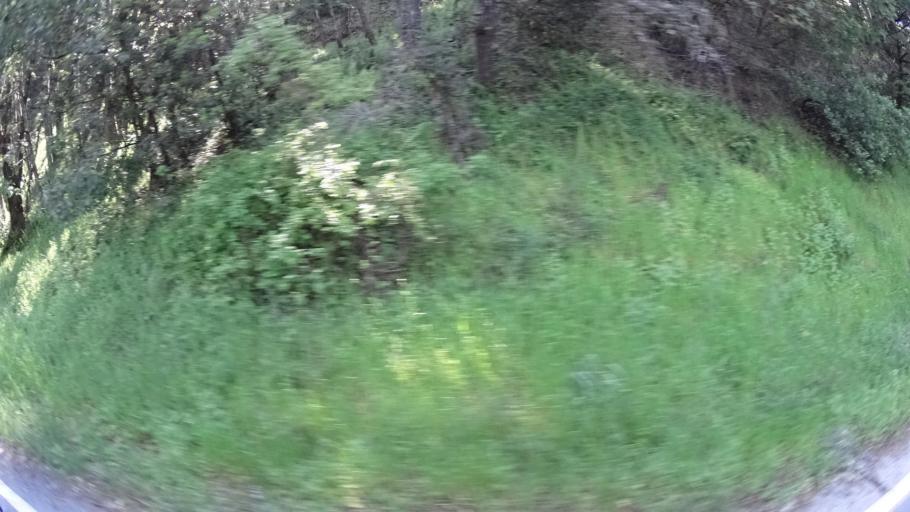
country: US
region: California
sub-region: Humboldt County
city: Redway
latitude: 40.1111
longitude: -123.7768
